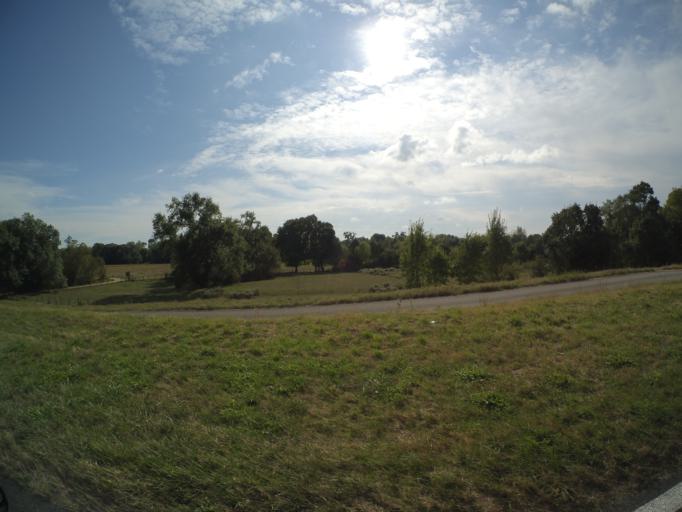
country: FR
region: Centre
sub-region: Departement d'Indre-et-Loire
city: Chouze-sur-Loire
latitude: 47.2419
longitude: 0.1433
